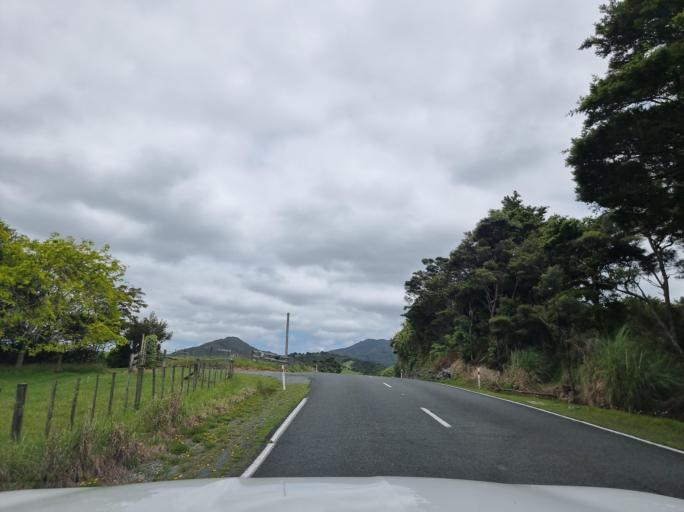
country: NZ
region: Auckland
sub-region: Auckland
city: Wellsford
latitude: -36.0861
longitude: 174.5416
